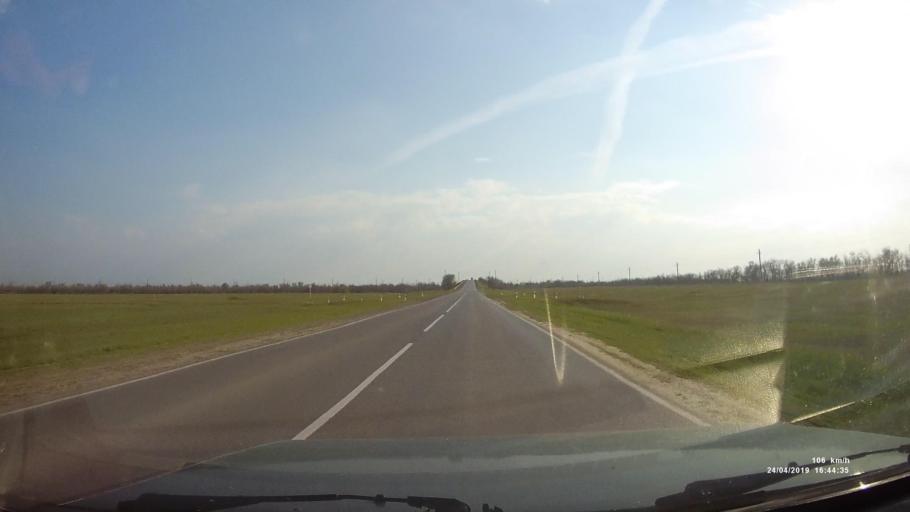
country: RU
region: Rostov
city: Gundorovskiy
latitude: 46.7799
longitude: 41.8251
